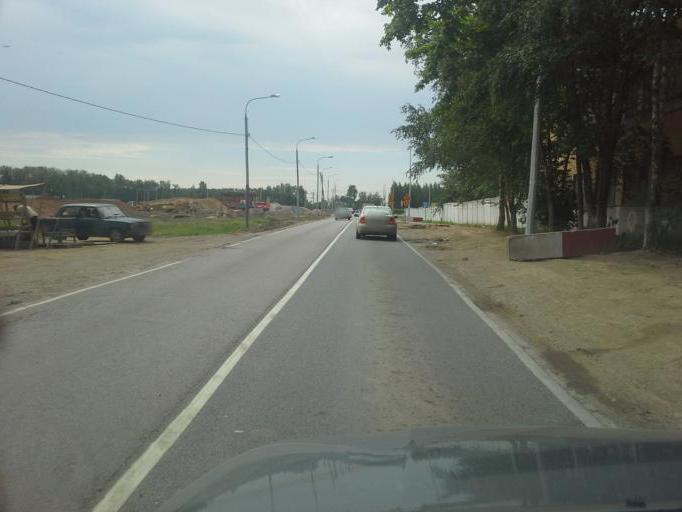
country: RU
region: Moskovskaya
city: Kokoshkino
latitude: 55.5858
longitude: 37.1216
